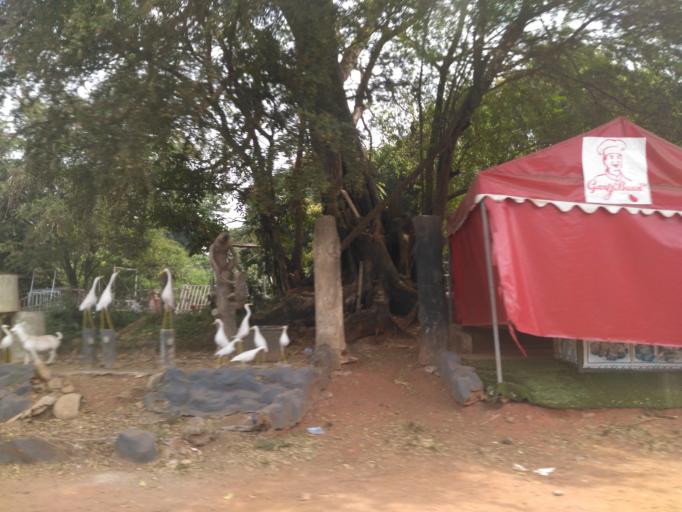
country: GH
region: Ashanti
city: Kumasi
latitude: 6.6796
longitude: -1.6439
